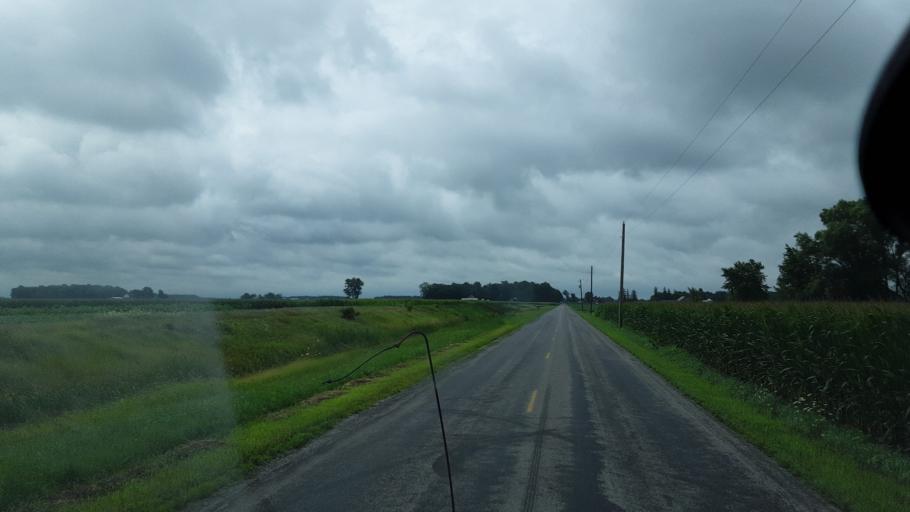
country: US
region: Indiana
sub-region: Wells County
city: Ossian
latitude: 40.8678
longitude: -85.1093
